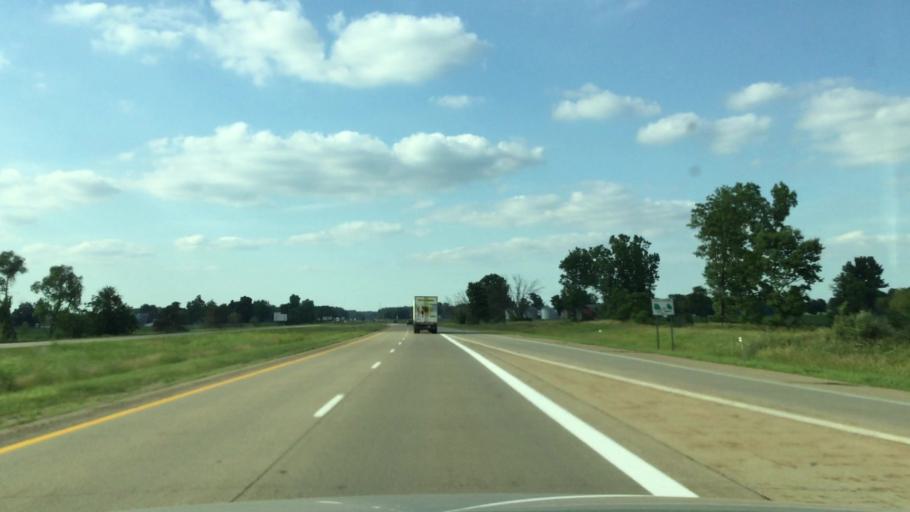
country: US
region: Michigan
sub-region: Branch County
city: Union City
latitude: 42.1101
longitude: -84.9954
